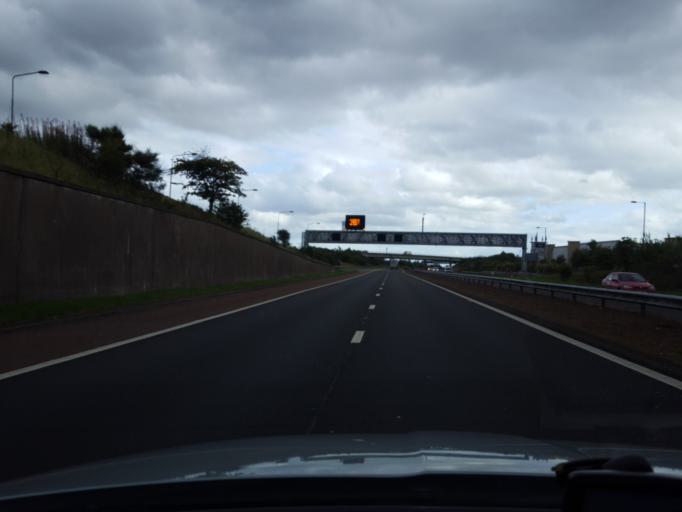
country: GB
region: Scotland
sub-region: Fife
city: Crossgates
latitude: 56.0809
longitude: -3.3969
